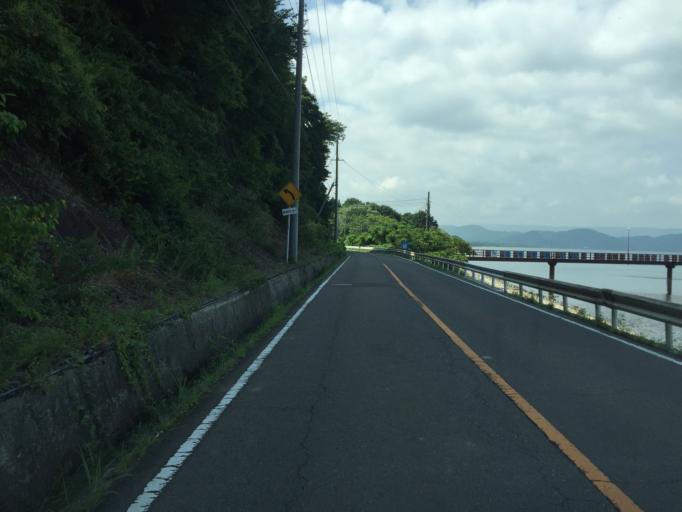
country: JP
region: Fukushima
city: Inawashiro
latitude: 37.4485
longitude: 140.1535
